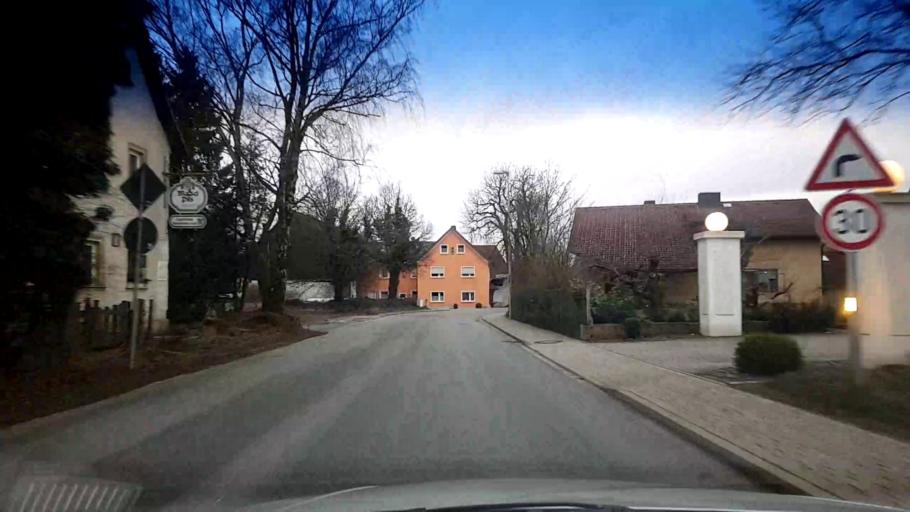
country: DE
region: Bavaria
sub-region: Upper Franconia
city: Wattendorf
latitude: 50.0444
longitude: 11.0940
